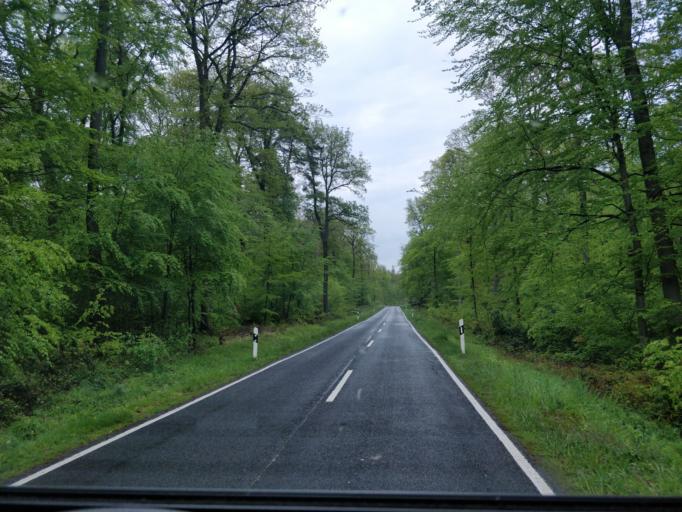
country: DE
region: North Rhine-Westphalia
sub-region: Regierungsbezirk Koln
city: Rheinbach
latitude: 50.5963
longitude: 6.9482
